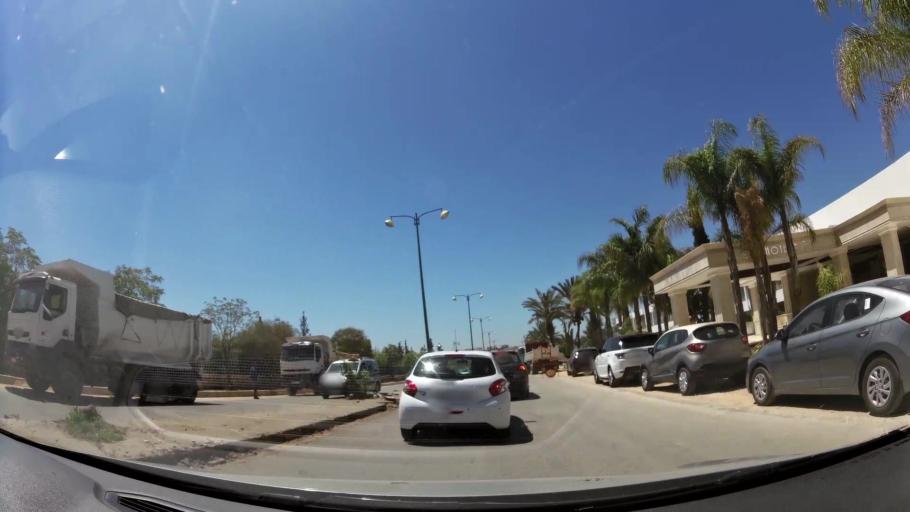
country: MA
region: Meknes-Tafilalet
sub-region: Meknes
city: Meknes
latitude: 33.8810
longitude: -5.5331
